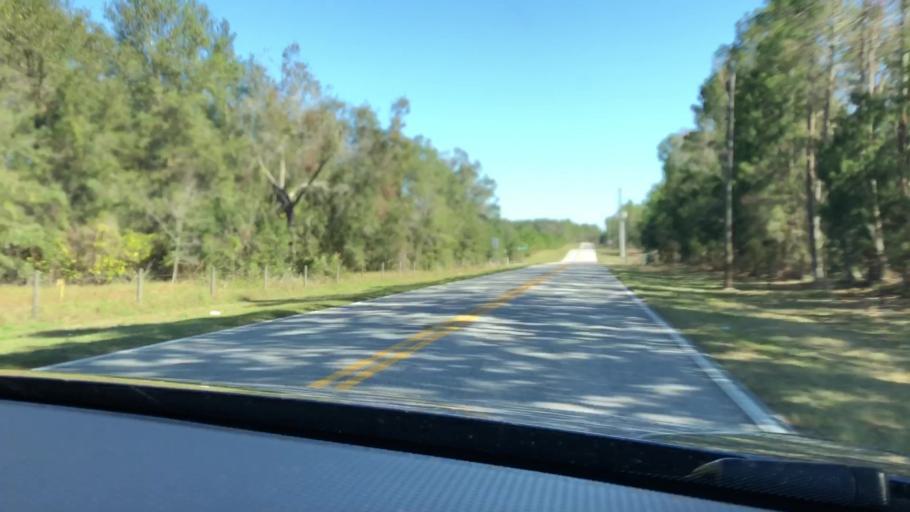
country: US
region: Florida
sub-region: Lake County
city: Eustis
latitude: 28.8725
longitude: -81.6277
